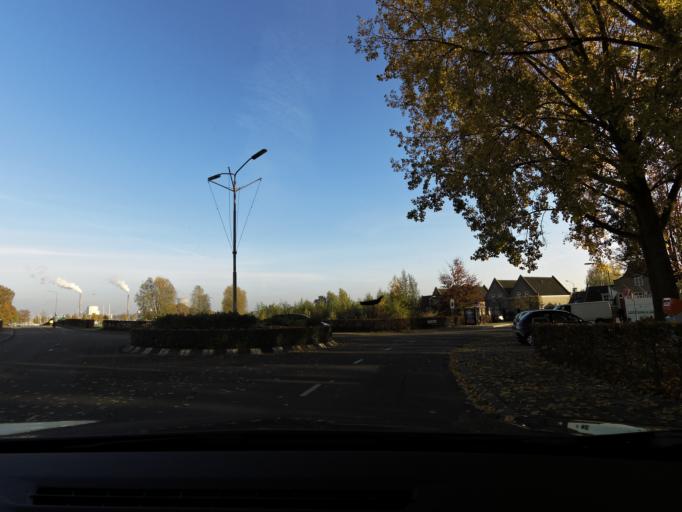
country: NL
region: North Brabant
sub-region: Gemeente Made en Drimmelen
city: Drimmelen
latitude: 51.7082
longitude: 4.8060
